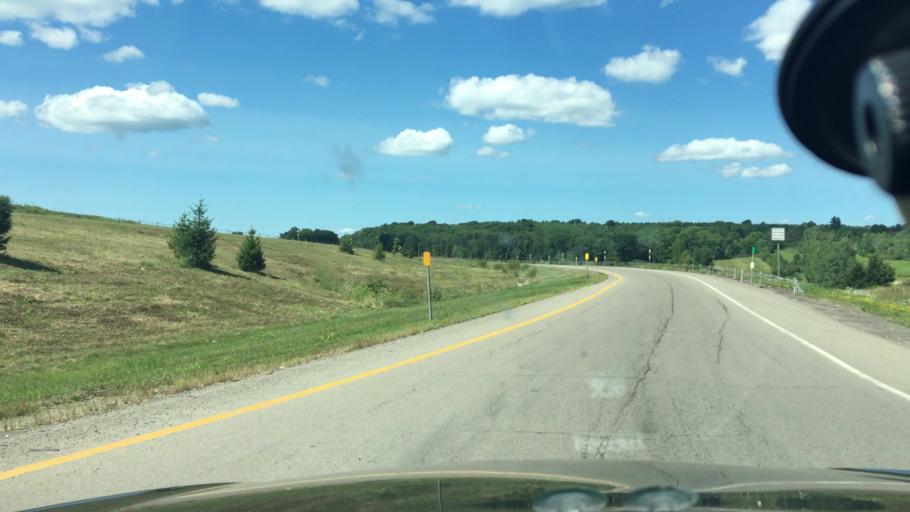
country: US
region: New York
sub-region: Erie County
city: Springville
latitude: 42.5097
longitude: -78.6908
